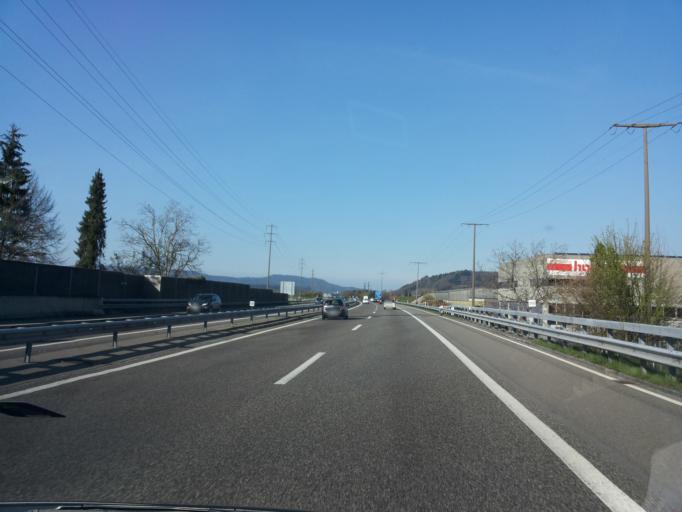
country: CH
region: Aargau
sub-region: Bezirk Zofingen
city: Kolliken
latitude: 47.3331
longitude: 8.0358
